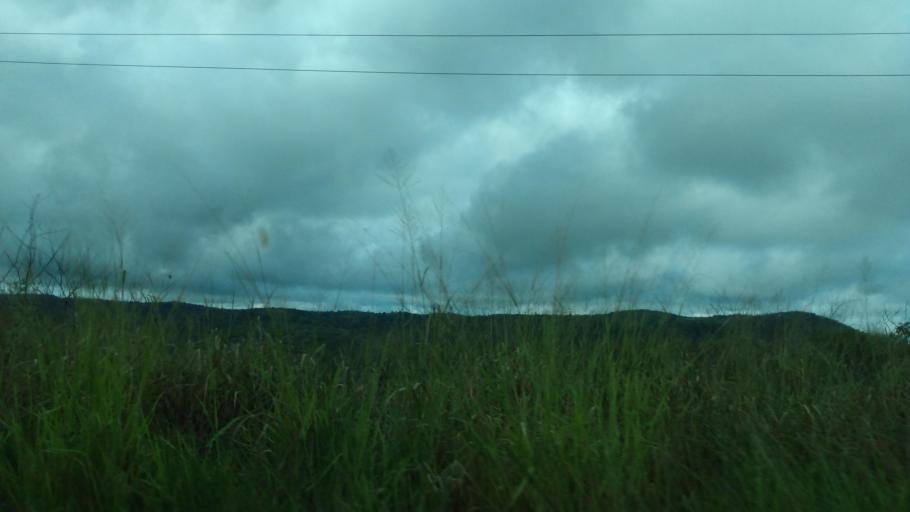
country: BR
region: Pernambuco
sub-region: Caruaru
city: Caruaru
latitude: -8.3172
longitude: -35.9787
